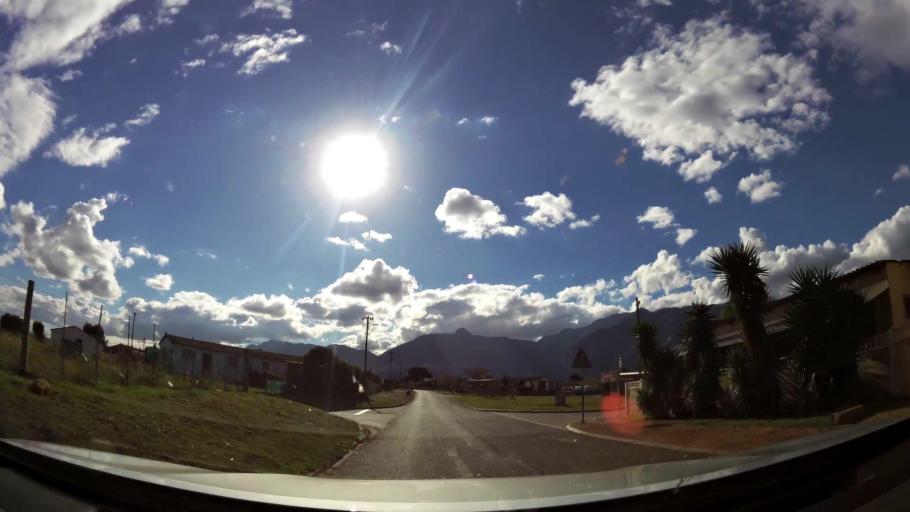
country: ZA
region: Western Cape
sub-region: Overberg District Municipality
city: Swellendam
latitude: -34.0409
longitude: 20.4411
